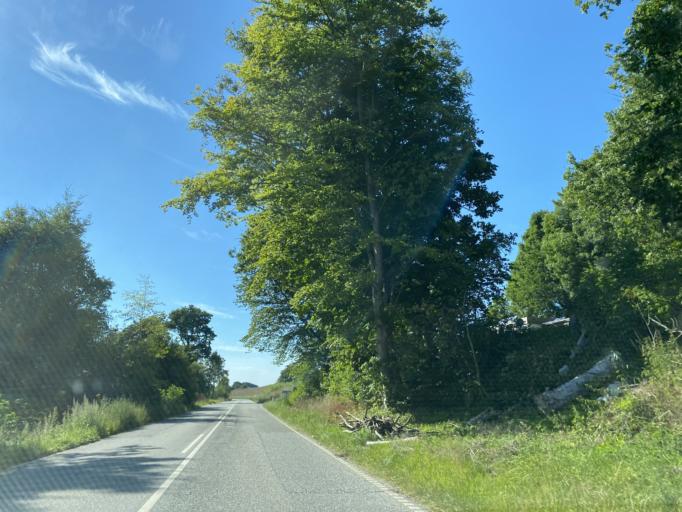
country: DK
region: Central Jutland
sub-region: Hedensted Kommune
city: Torring
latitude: 55.8234
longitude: 9.4530
